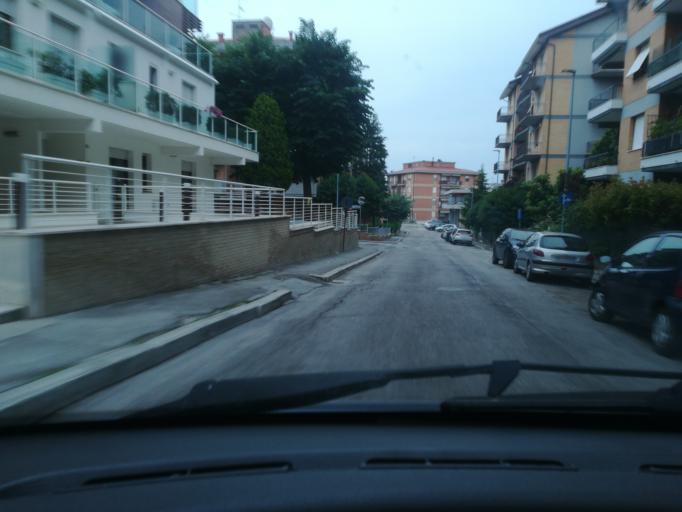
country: IT
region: The Marches
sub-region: Provincia di Macerata
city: Macerata
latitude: 43.2942
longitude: 13.4457
